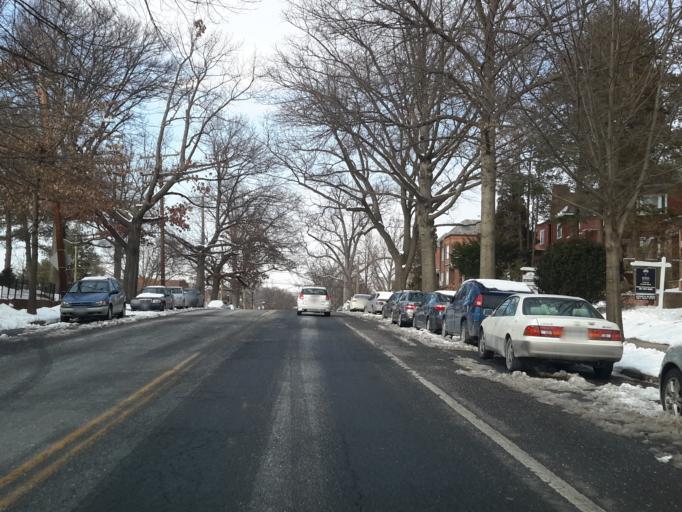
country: US
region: Maryland
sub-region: Montgomery County
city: Silver Spring
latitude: 38.9644
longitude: -77.0334
